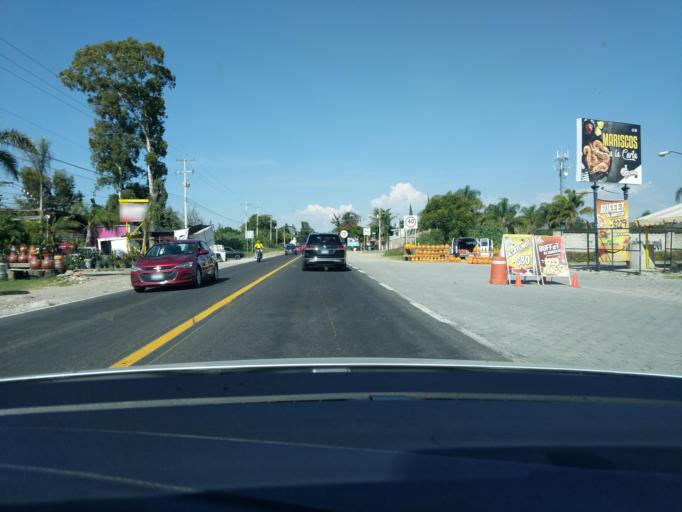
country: MX
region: Puebla
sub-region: Atlixco
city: San Agustin Huixaxtla
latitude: 18.9391
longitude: -98.3999
